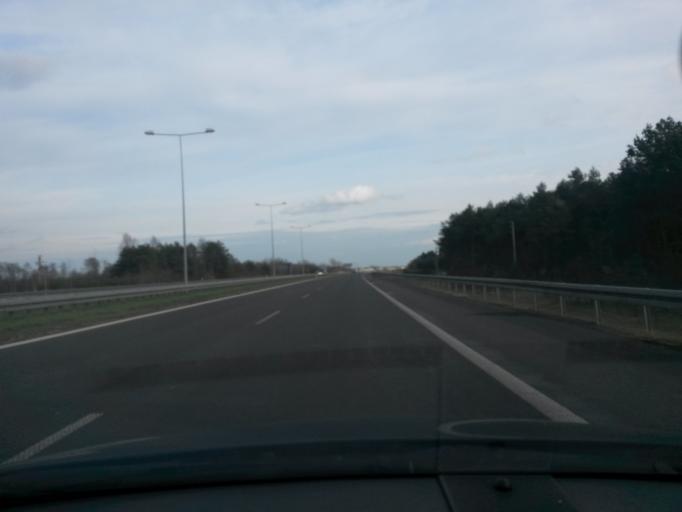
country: PL
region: Greater Poland Voivodeship
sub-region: Powiat kolski
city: Dabie
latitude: 52.0663
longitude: 18.8239
